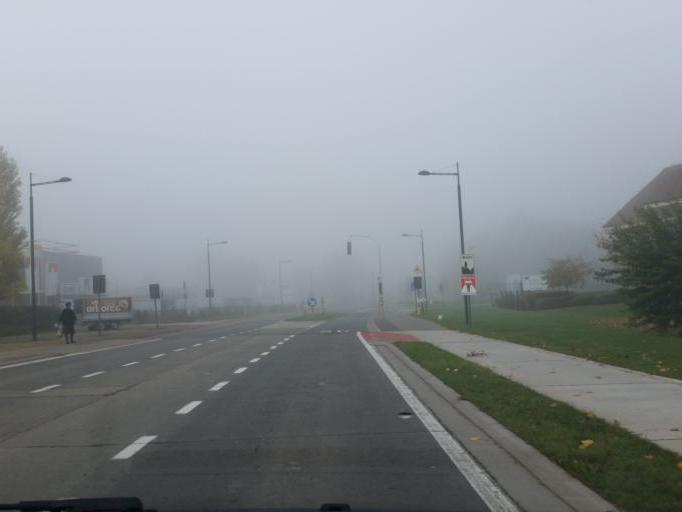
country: BE
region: Flanders
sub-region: Provincie Oost-Vlaanderen
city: Melle
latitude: 50.9977
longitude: 3.8120
